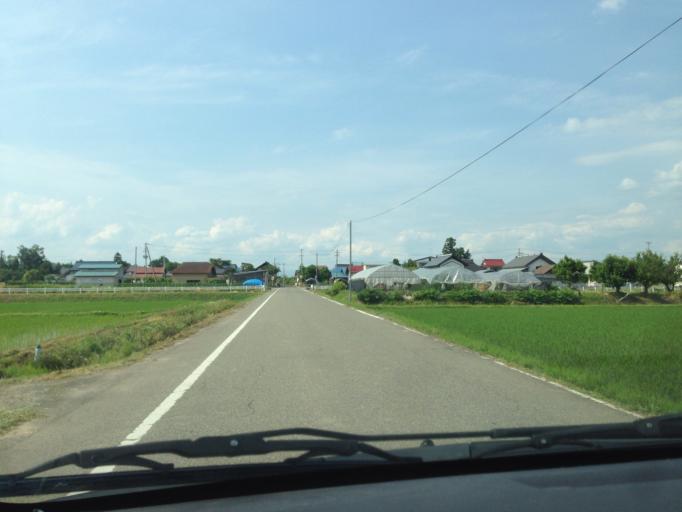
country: JP
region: Fukushima
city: Kitakata
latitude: 37.5044
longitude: 139.8298
